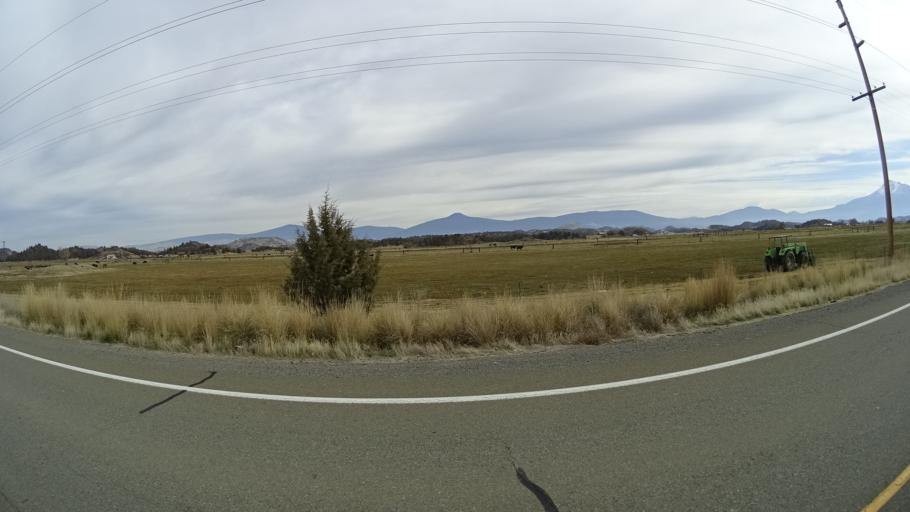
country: US
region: California
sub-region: Siskiyou County
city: Montague
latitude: 41.6659
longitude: -122.5224
